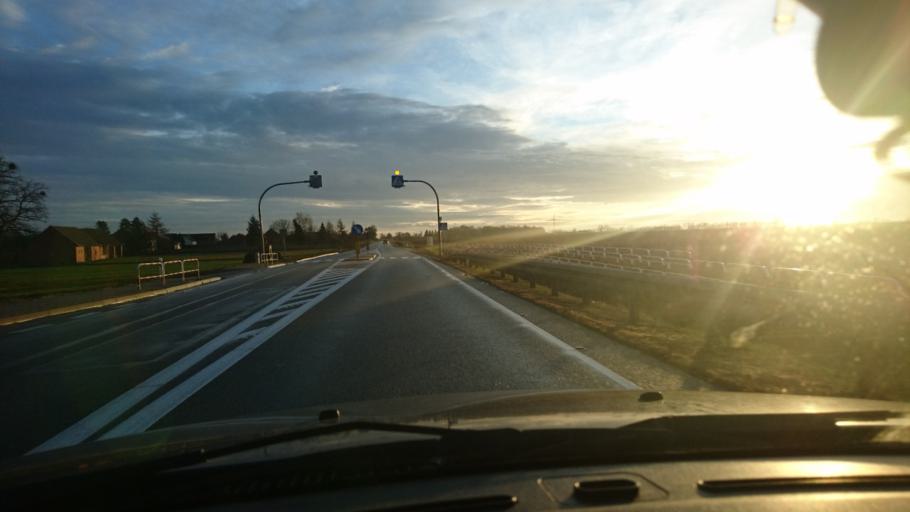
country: PL
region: Greater Poland Voivodeship
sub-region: Powiat kepinski
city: Opatow
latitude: 51.1921
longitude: 18.1480
